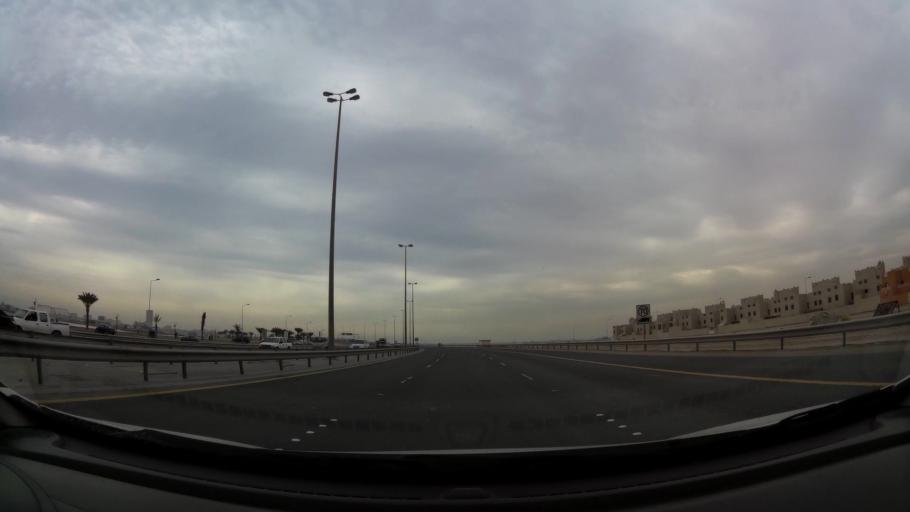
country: BH
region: Manama
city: Manama
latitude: 26.1807
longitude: 50.5914
